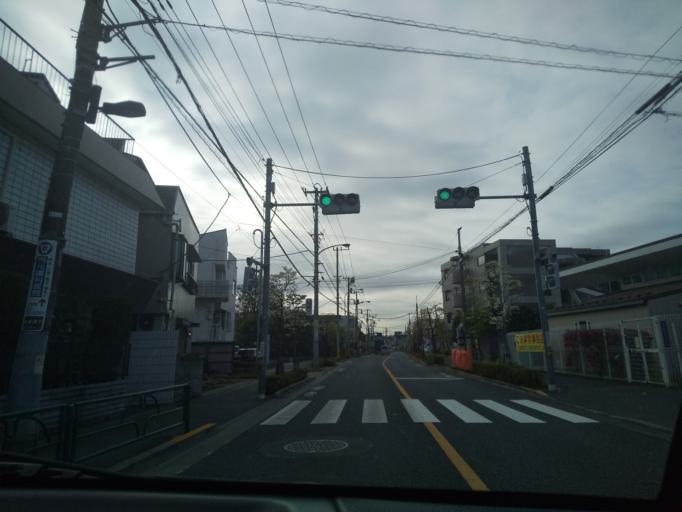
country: JP
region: Tokyo
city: Kokubunji
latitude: 35.7032
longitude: 139.4884
